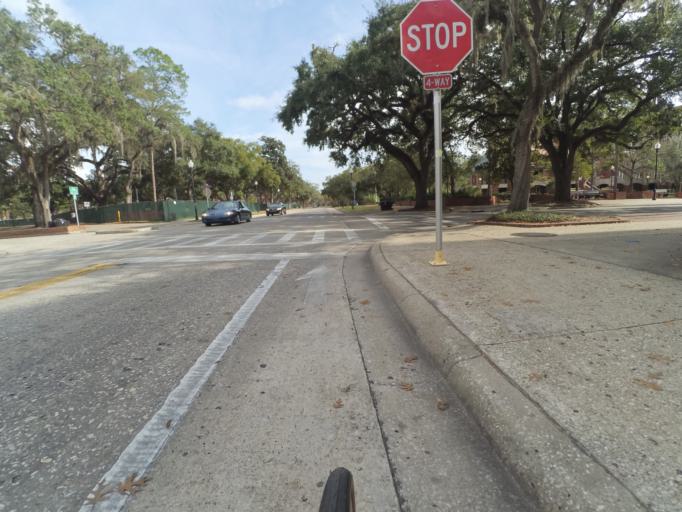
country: US
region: Florida
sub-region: Alachua County
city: Gainesville
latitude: 29.6497
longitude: -82.3438
